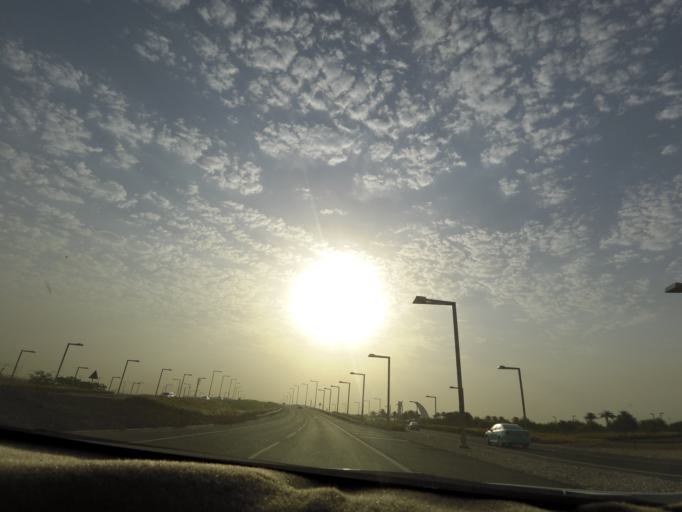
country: QA
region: Al Wakrah
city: Al Wakrah
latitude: 25.2476
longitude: 51.6100
